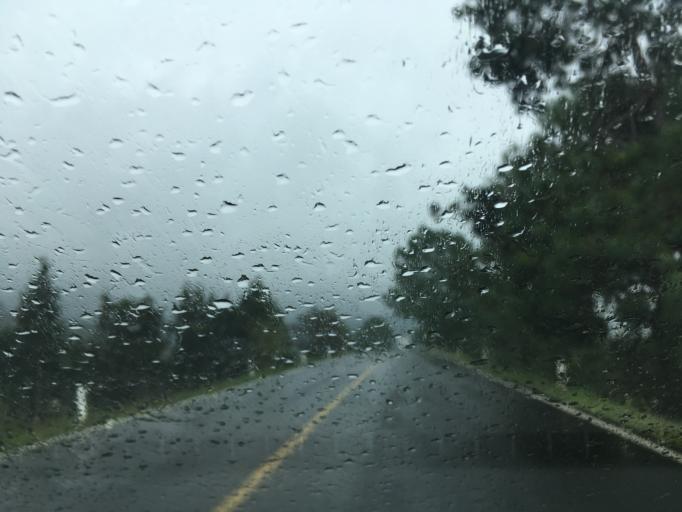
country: MX
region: Michoacan
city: Tingambato
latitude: 19.5040
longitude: -101.8643
